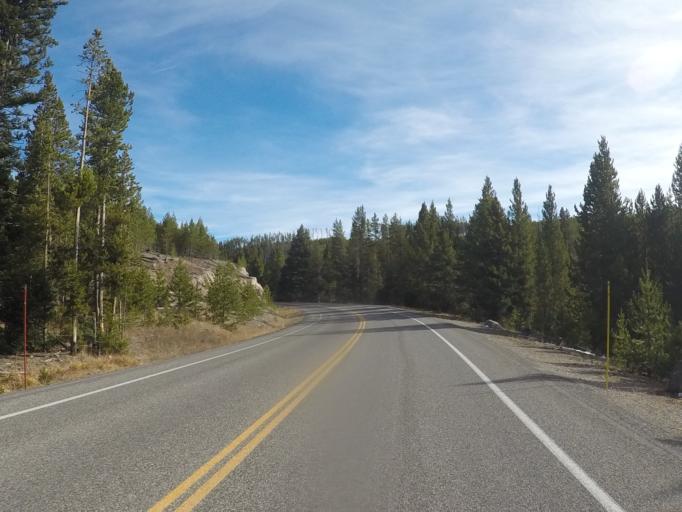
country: US
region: Montana
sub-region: Gallatin County
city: West Yellowstone
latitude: 44.6499
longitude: -110.7986
